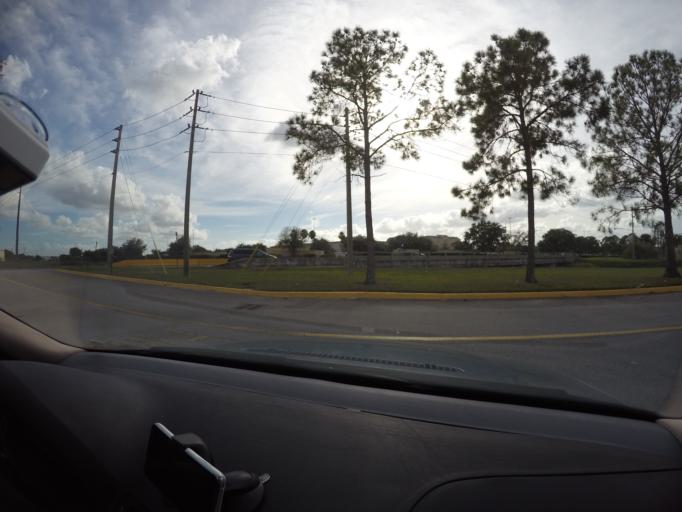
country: US
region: Florida
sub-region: Orange County
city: Sky Lake
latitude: 28.4490
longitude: -81.3913
